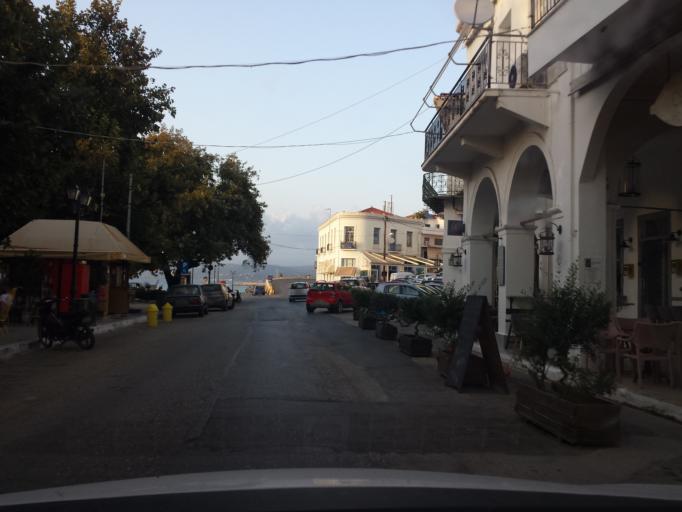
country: GR
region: Peloponnese
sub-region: Nomos Messinias
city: Pylos
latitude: 36.9136
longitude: 21.6967
